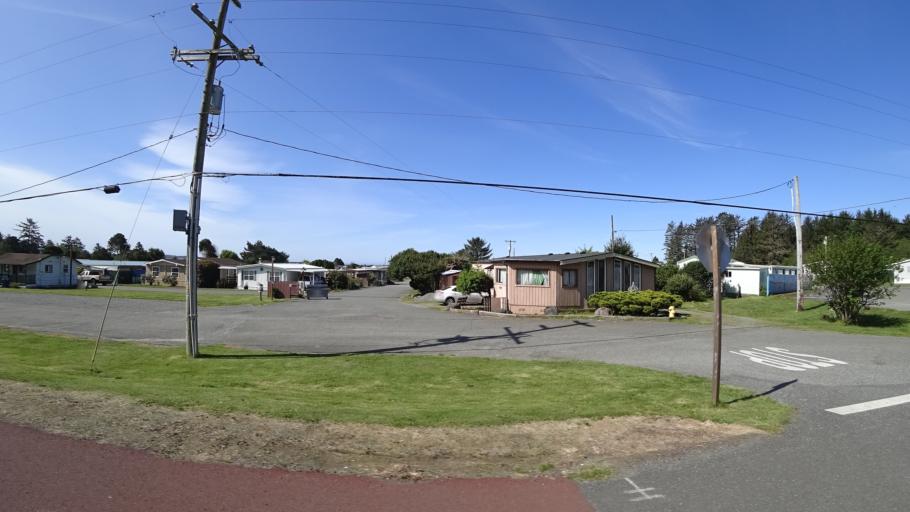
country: US
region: Oregon
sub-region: Curry County
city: Harbor
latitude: 41.9479
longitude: -124.1970
